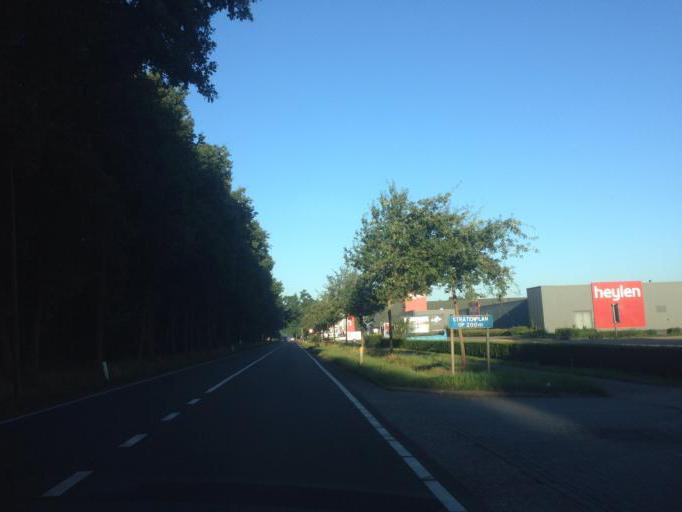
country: BE
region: Flanders
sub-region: Provincie Limburg
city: Peer
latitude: 51.1355
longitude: 5.5018
